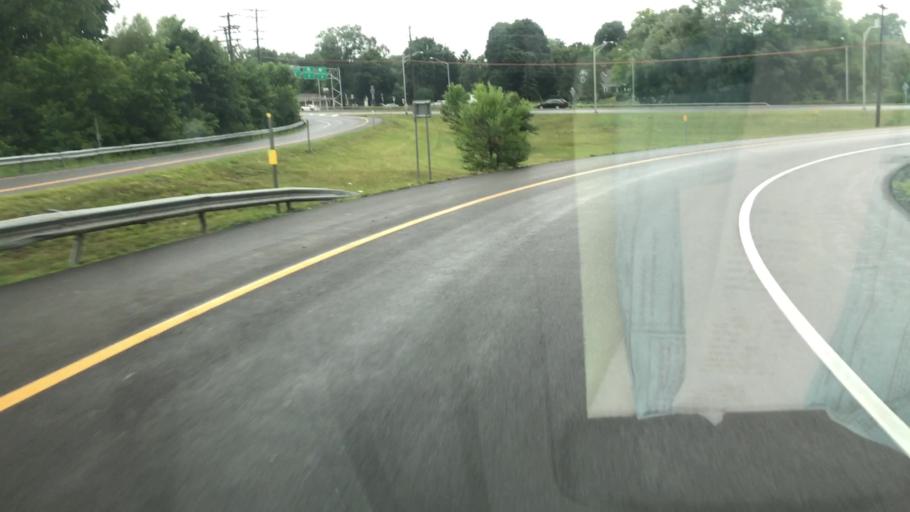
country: US
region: New York
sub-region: Onondaga County
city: East Syracuse
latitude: 43.0330
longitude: -76.0622
